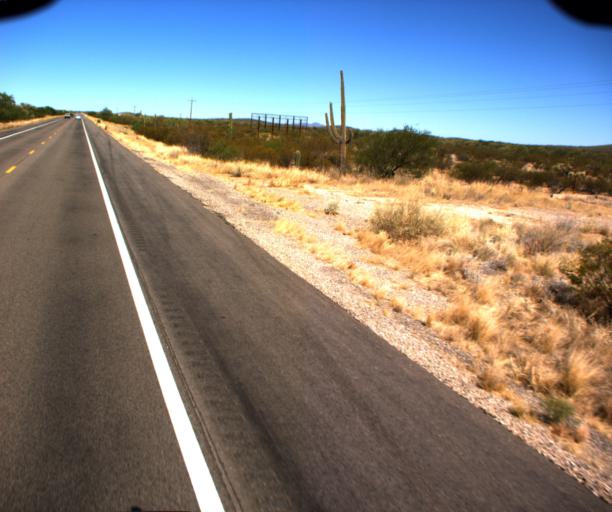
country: US
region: Arizona
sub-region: Pima County
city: Three Points
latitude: 32.0403
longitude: -111.4730
